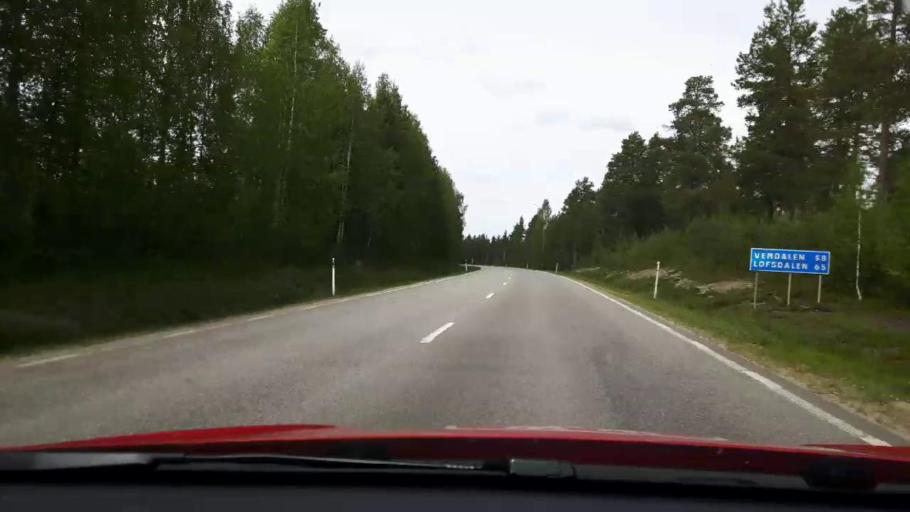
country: SE
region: Jaemtland
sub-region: Harjedalens Kommun
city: Sveg
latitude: 62.0402
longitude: 14.3612
